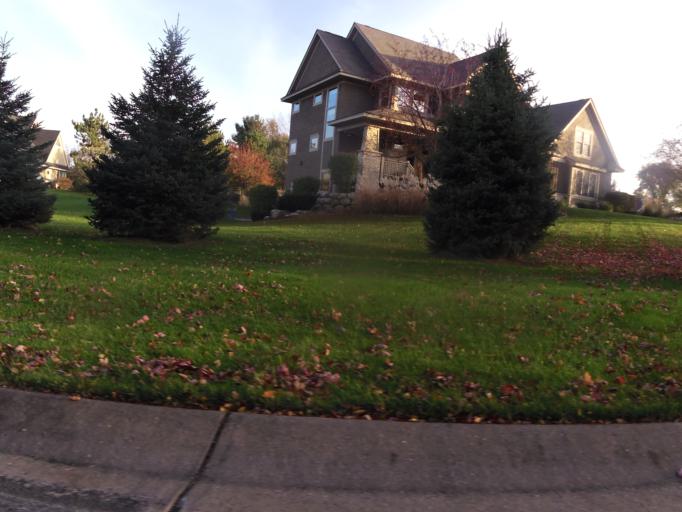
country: US
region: Minnesota
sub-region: Washington County
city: Lake Elmo
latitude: 44.9699
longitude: -92.8805
